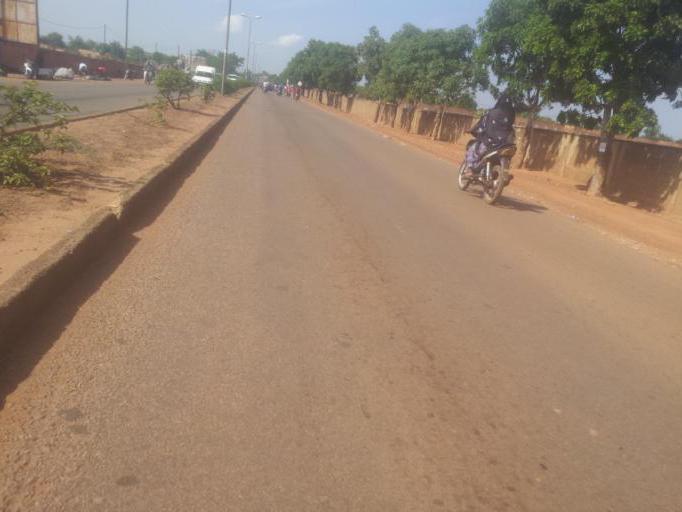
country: BF
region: Centre
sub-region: Kadiogo Province
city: Ouagadougou
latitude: 12.3650
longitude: -1.5586
